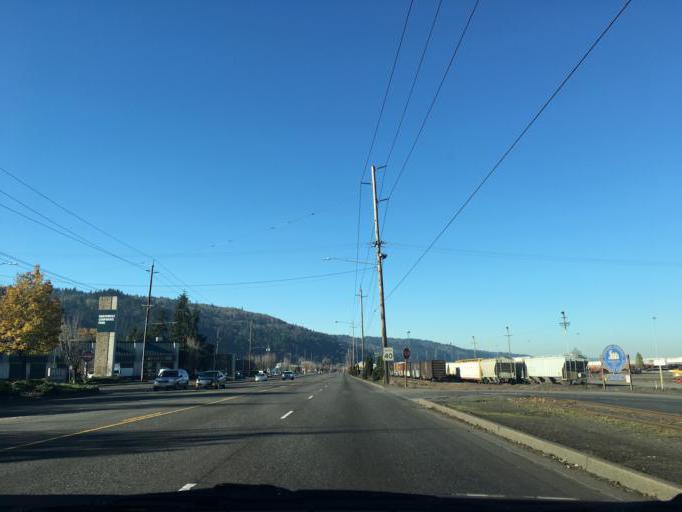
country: US
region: Oregon
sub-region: Multnomah County
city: Portland
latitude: 45.5472
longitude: -122.7127
